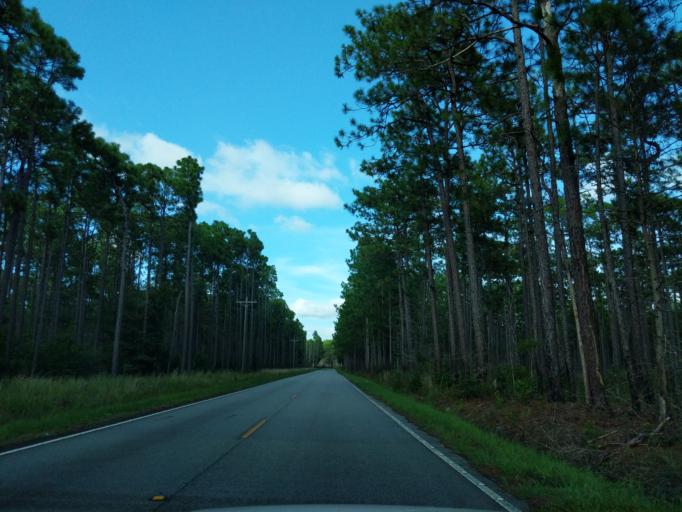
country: US
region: South Carolina
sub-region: Charleston County
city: Awendaw
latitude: 33.1352
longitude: -79.4361
